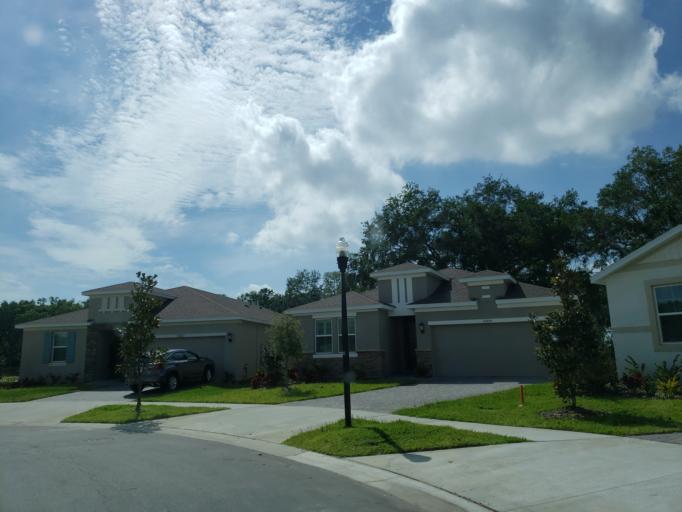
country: US
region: Florida
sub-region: Hillsborough County
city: Riverview
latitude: 27.8986
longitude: -82.3213
